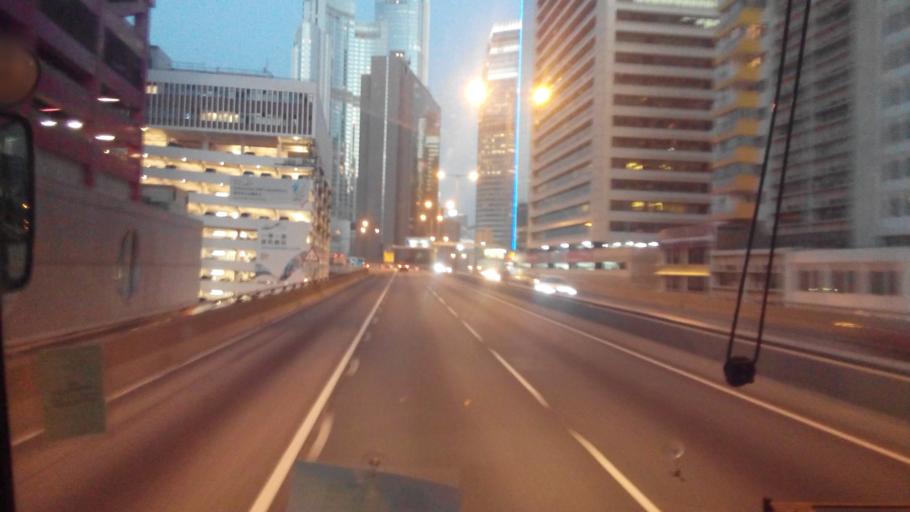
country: HK
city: Hong Kong
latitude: 22.2876
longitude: 114.1519
